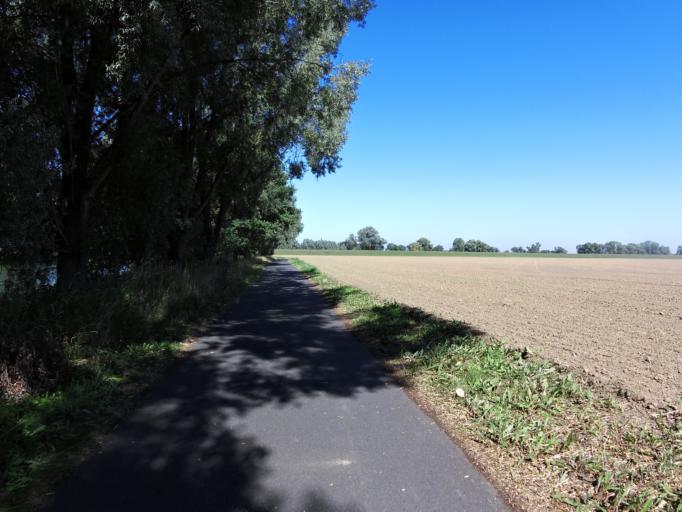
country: DE
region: Saxony-Anhalt
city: Pretzsch
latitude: 51.7062
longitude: 12.8201
